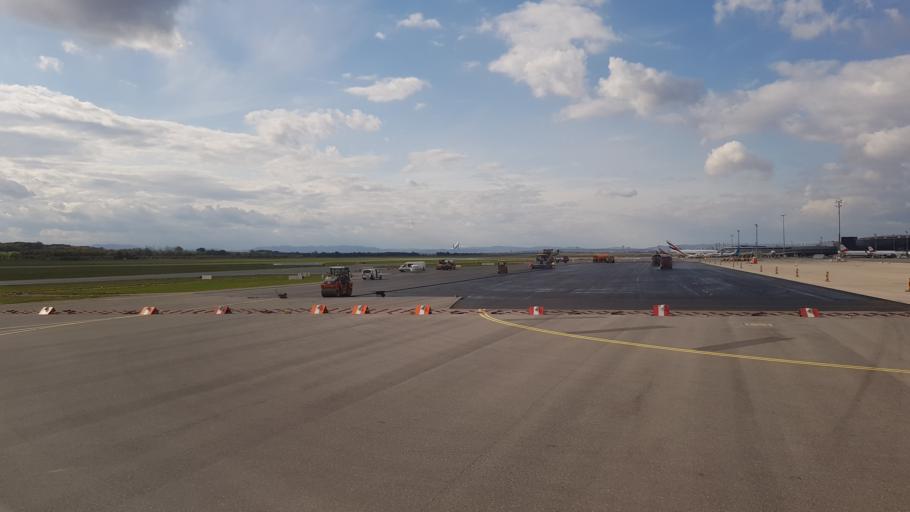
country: AT
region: Lower Austria
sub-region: Politischer Bezirk Bruck an der Leitha
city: Enzersdorf an der Fischa
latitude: 48.1131
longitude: 16.5732
